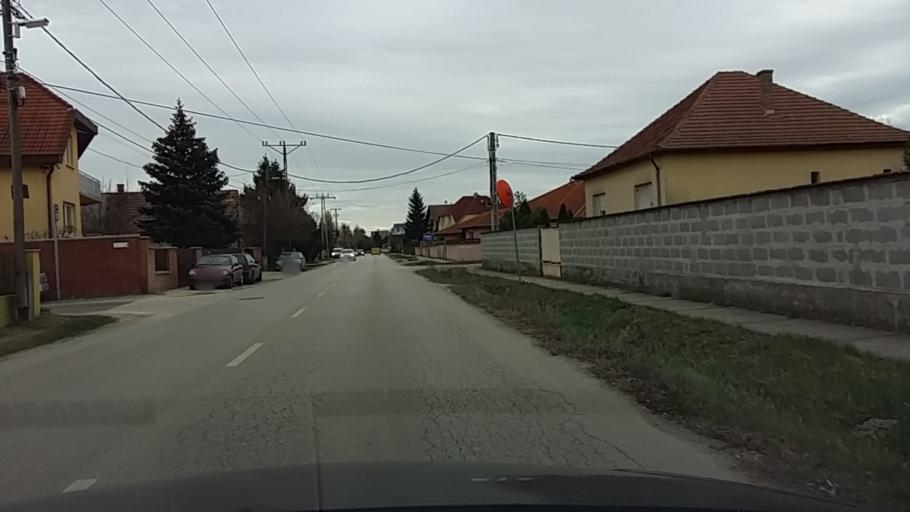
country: HU
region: Pest
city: Szigetszentmiklos
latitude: 47.3570
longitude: 19.0330
